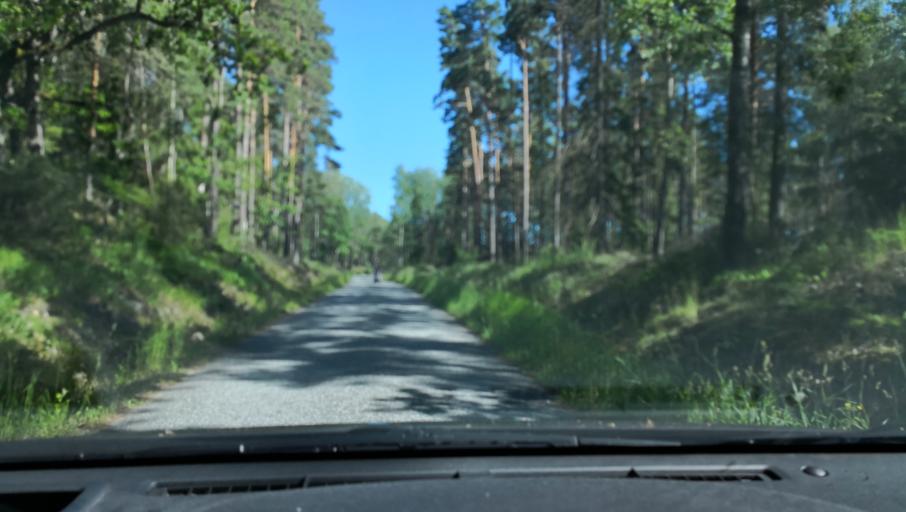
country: SE
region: Soedermanland
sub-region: Eskilstuna Kommun
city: Eskilstuna
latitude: 59.3455
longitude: 16.5548
